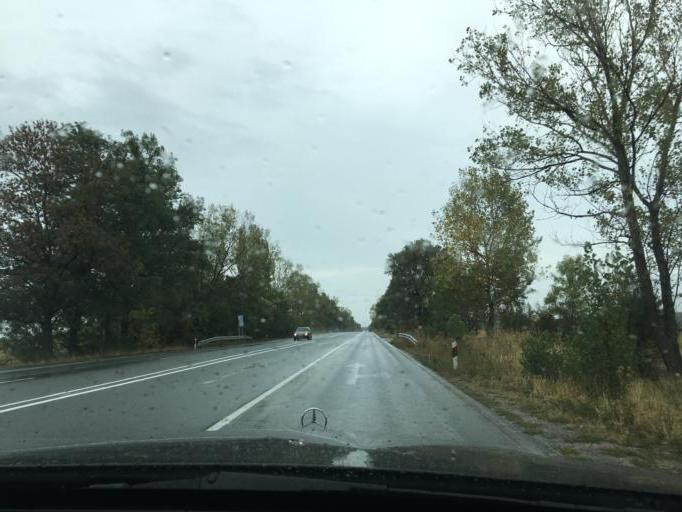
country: BG
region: Sofiya
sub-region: Obshtina Slivnitsa
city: Slivnitsa
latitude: 42.8121
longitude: 23.1164
